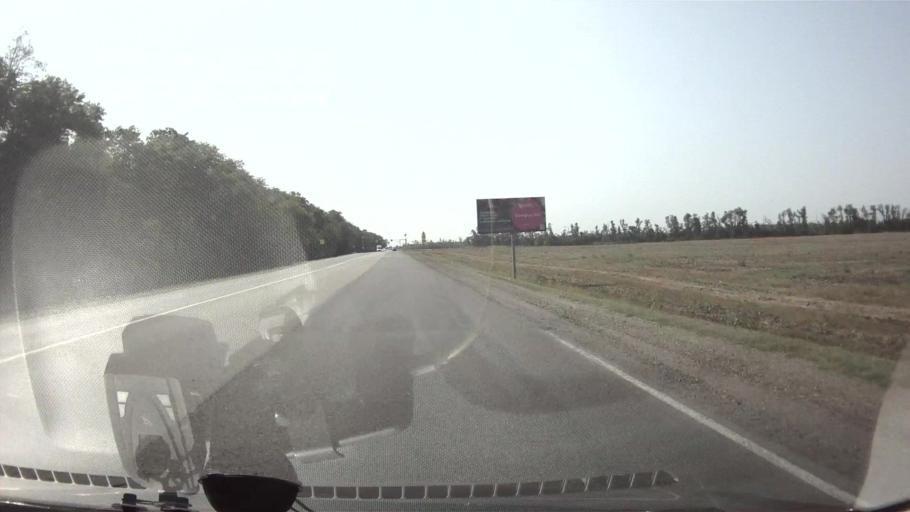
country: RU
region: Krasnodarskiy
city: Vasyurinskaya
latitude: 45.1681
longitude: 39.4746
